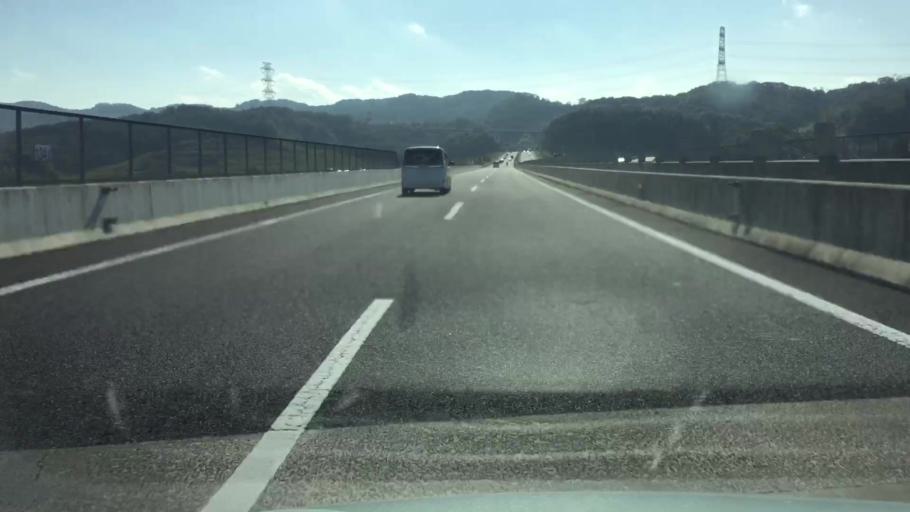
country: JP
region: Tochigi
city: Mooka
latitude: 36.3866
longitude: 140.0238
